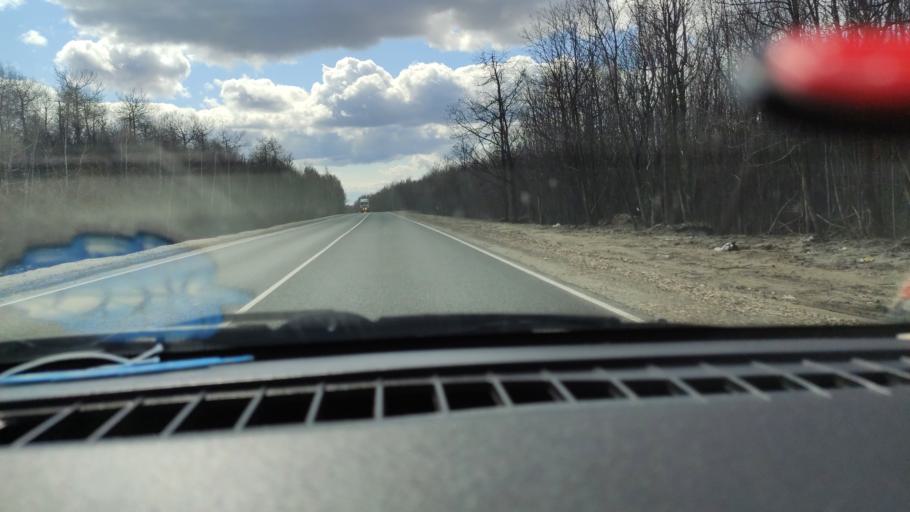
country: RU
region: Saratov
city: Khvalynsk
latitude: 52.4712
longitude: 48.0154
